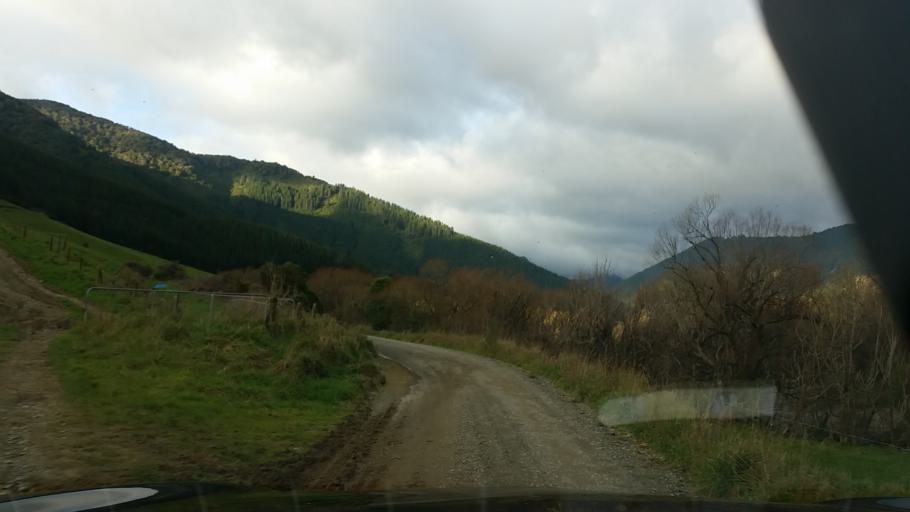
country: NZ
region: Nelson
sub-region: Nelson City
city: Nelson
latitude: -41.2104
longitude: 173.6307
